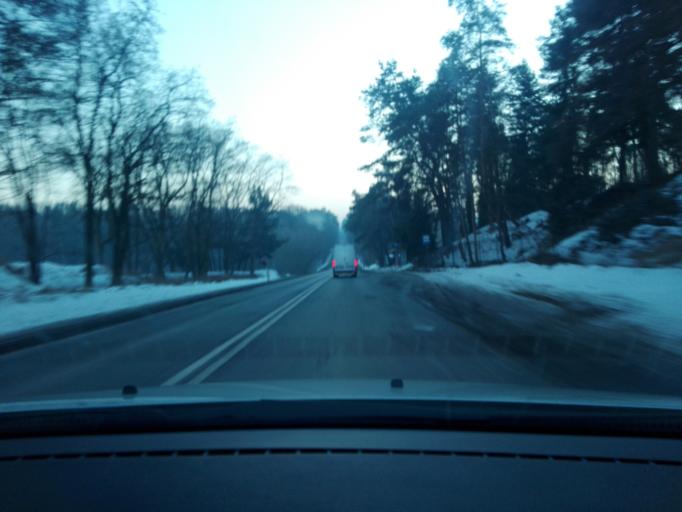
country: PL
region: Lodz Voivodeship
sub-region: Powiat zgierski
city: Zgierz
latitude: 51.8854
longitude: 19.4160
